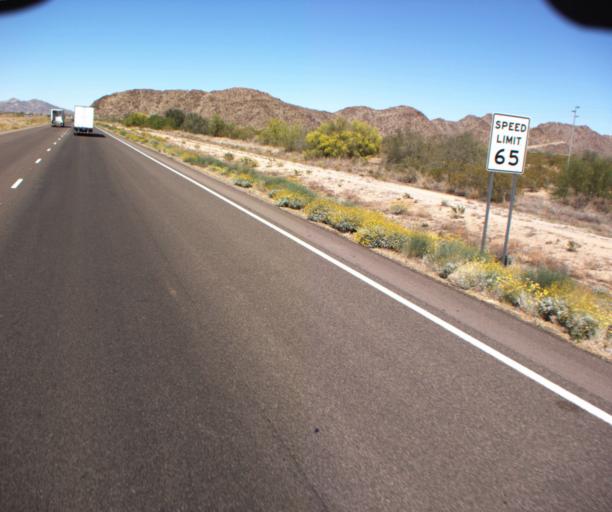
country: US
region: Arizona
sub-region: Maricopa County
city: Buckeye
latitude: 33.1620
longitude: -112.6499
